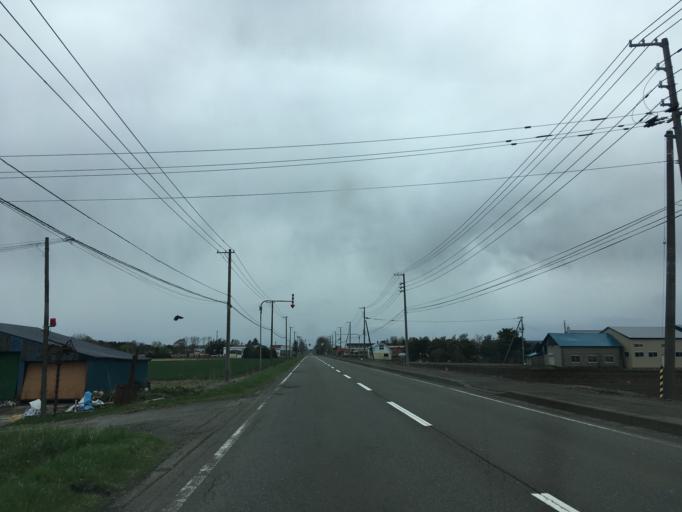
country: JP
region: Hokkaido
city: Chitose
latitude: 42.9357
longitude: 141.8058
